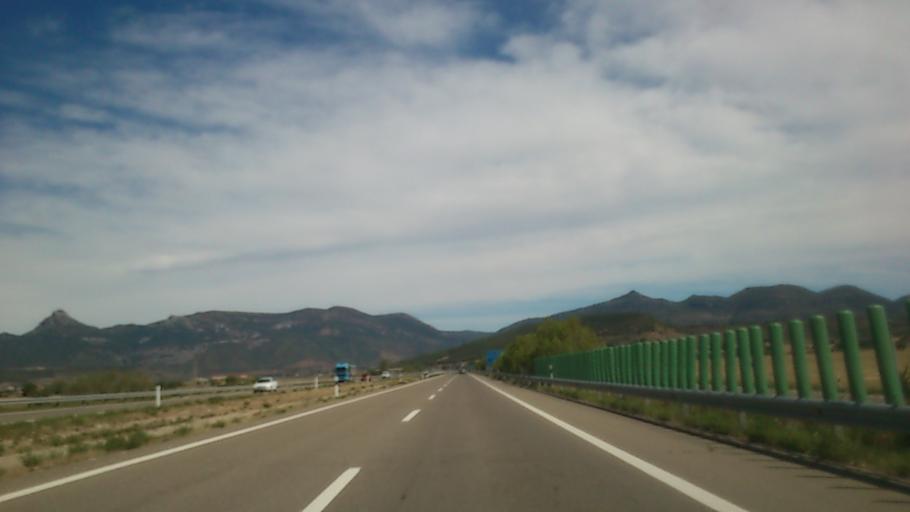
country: ES
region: Aragon
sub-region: Provincia de Huesca
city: Igries
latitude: 42.1976
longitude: -0.4361
